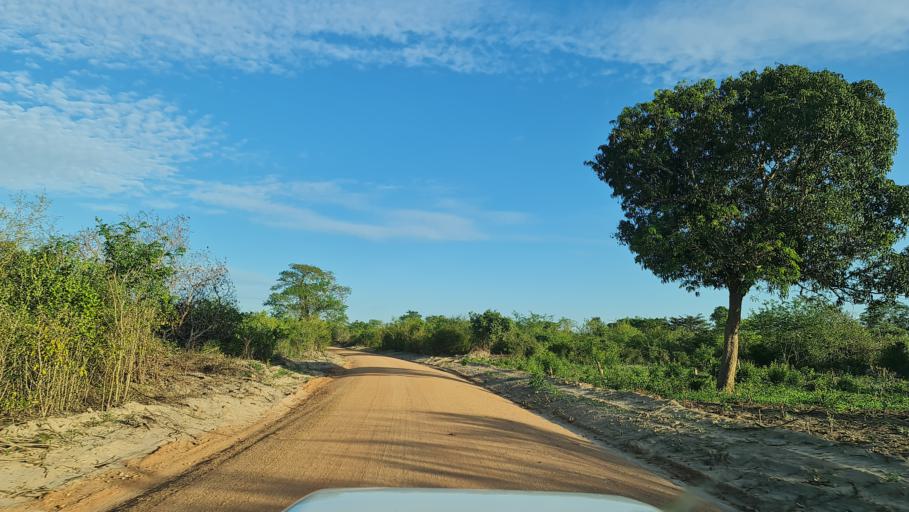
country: MZ
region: Nampula
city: Nacala
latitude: -14.6834
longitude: 40.3002
